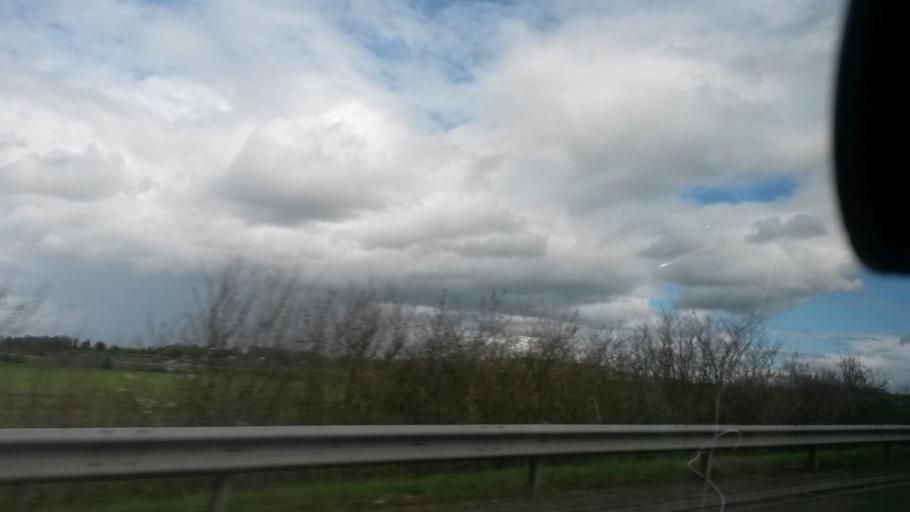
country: IE
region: Leinster
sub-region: Kildare
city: Cherryville
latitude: 53.1495
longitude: -6.9912
